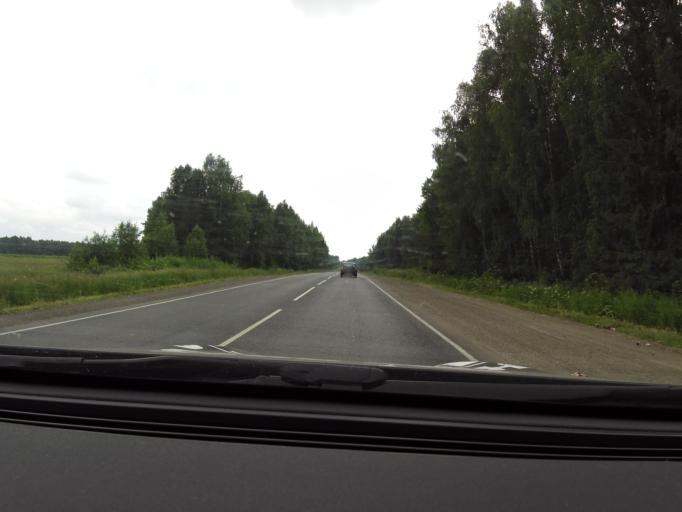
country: RU
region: Perm
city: Kungur
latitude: 57.4401
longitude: 56.8187
